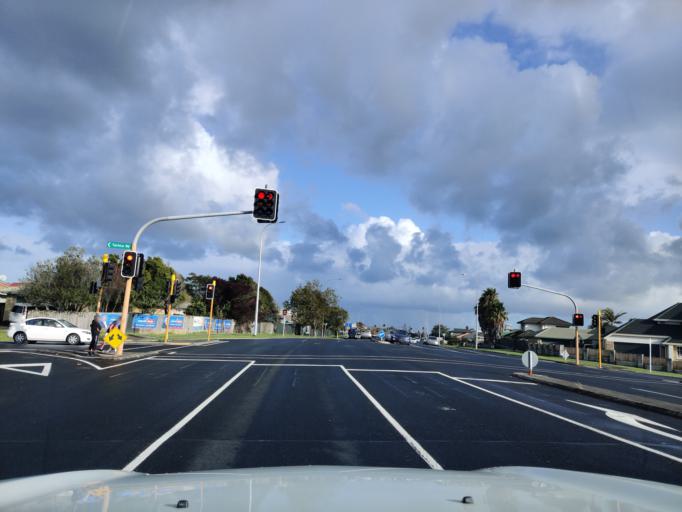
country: NZ
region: Auckland
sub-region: Auckland
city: Pakuranga
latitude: -36.9259
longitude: 174.9131
